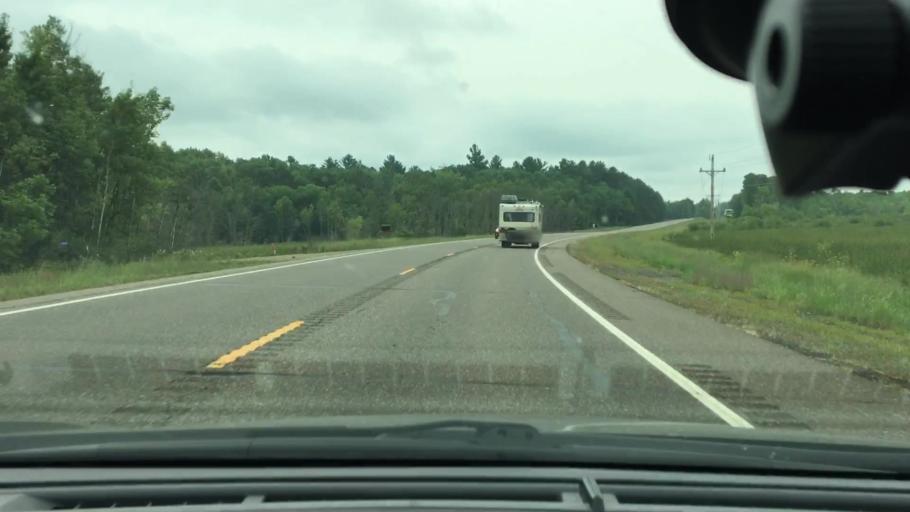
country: US
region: Minnesota
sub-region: Crow Wing County
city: Crosby
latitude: 46.5038
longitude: -93.9568
